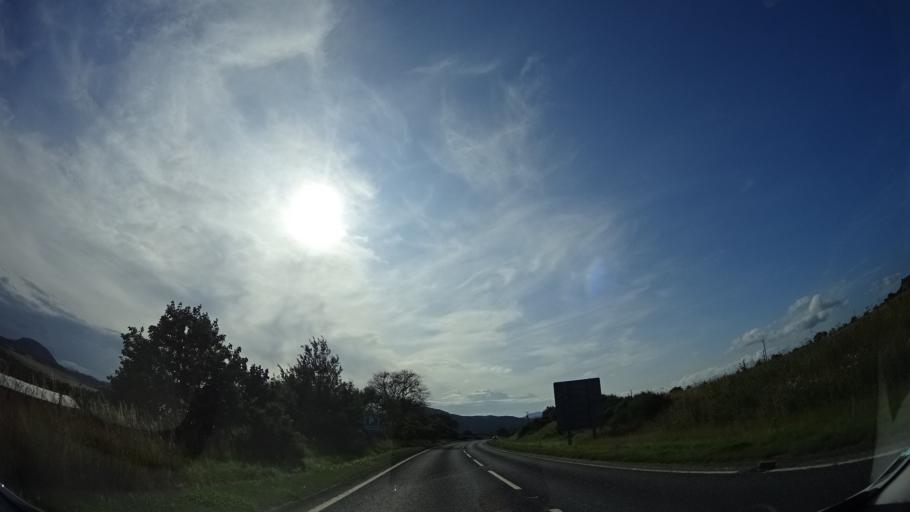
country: GB
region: Scotland
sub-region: Highland
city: Muir of Ord
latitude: 57.5579
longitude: -4.5412
